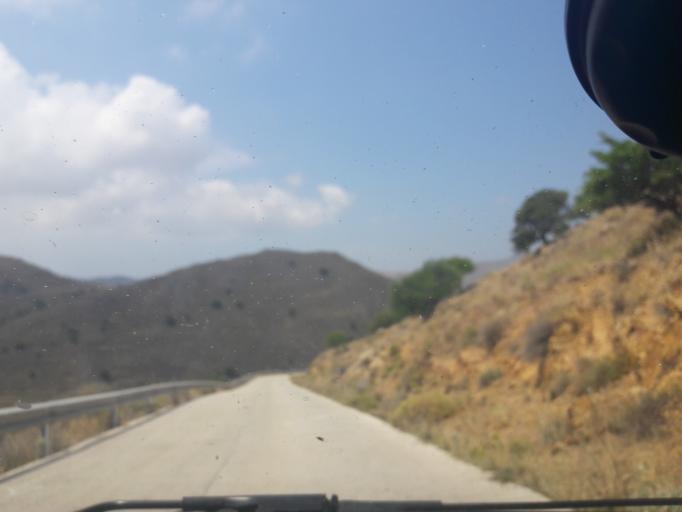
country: GR
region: North Aegean
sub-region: Nomos Lesvou
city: Myrina
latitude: 39.9668
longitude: 25.1526
